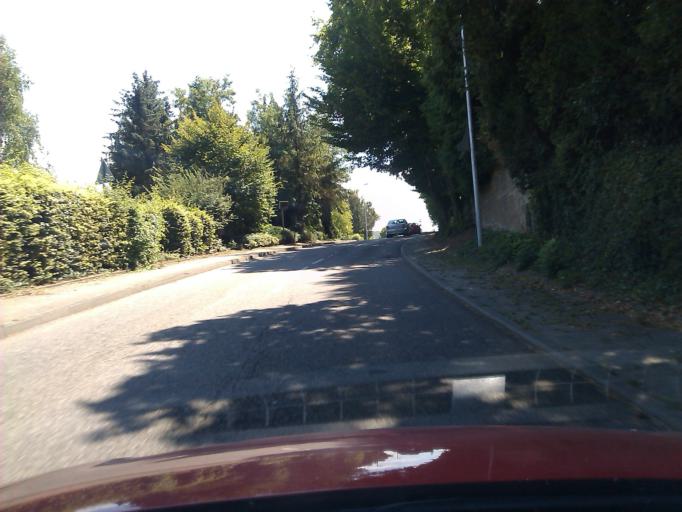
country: DE
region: Baden-Wuerttemberg
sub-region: Regierungsbezirk Stuttgart
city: Schwaigern
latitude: 49.1370
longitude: 9.0629
